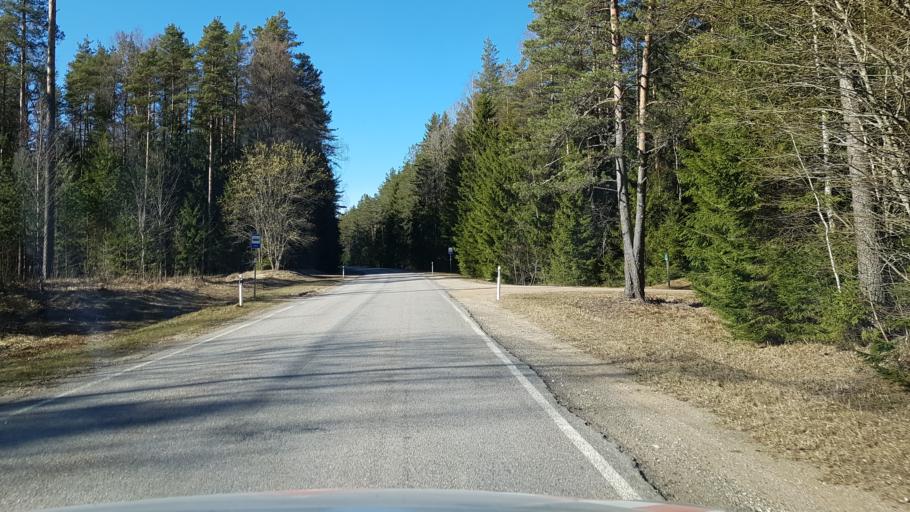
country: EE
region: Laeaene-Virumaa
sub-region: Vinni vald
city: Vinni
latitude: 59.2552
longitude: 26.6870
